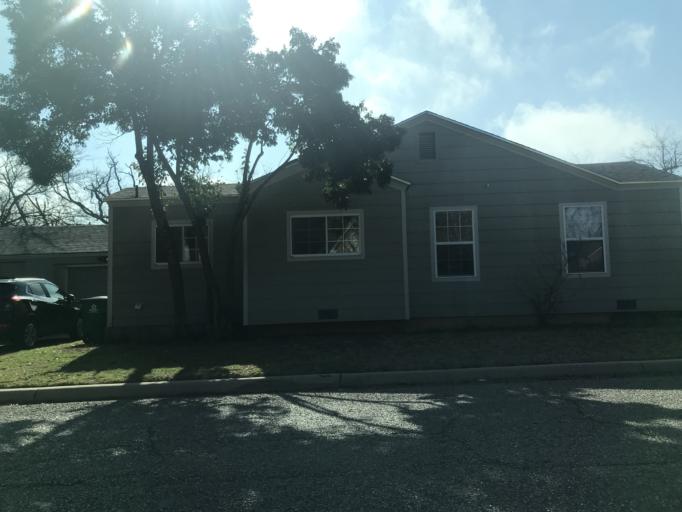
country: US
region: Texas
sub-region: Tom Green County
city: San Angelo
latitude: 31.4522
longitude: -100.4536
